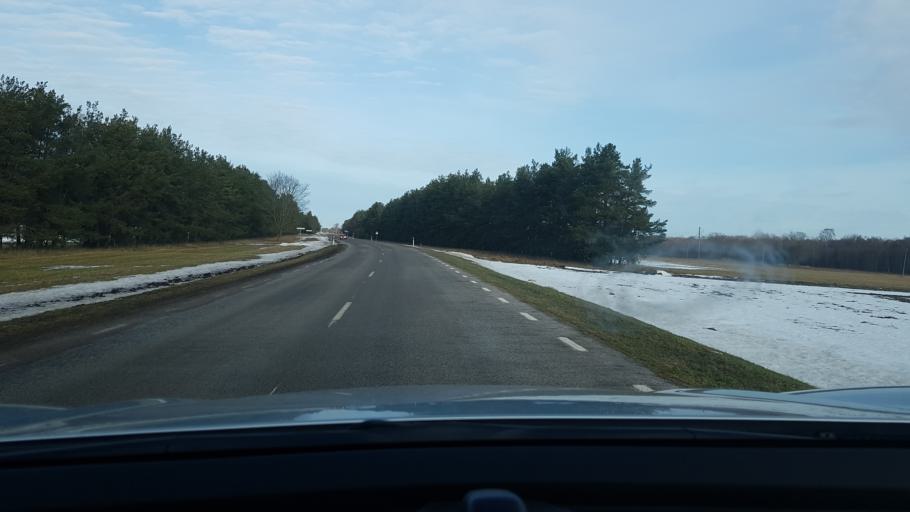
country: EE
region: Saare
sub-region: Kuressaare linn
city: Kuressaare
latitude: 58.5099
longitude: 22.7062
